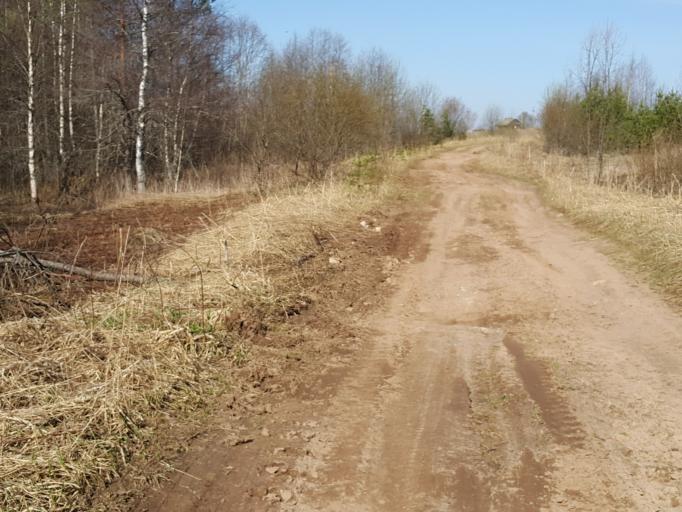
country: RU
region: Leningrad
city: Podporozh'ye
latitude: 60.3540
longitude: 34.8414
